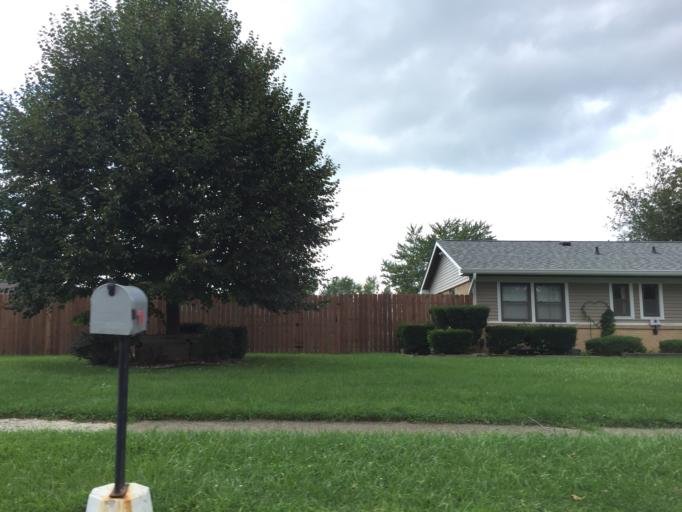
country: US
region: Indiana
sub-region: Howard County
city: Kokomo
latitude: 40.4666
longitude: -86.1045
